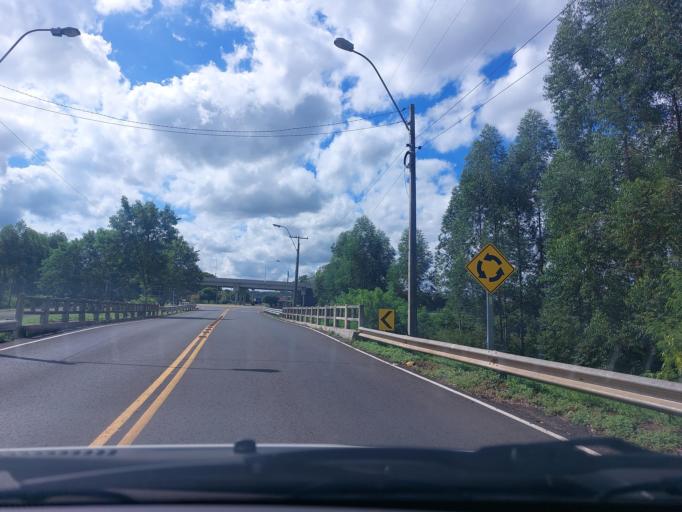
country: PY
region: San Pedro
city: Guayaybi
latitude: -24.6033
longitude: -56.4900
